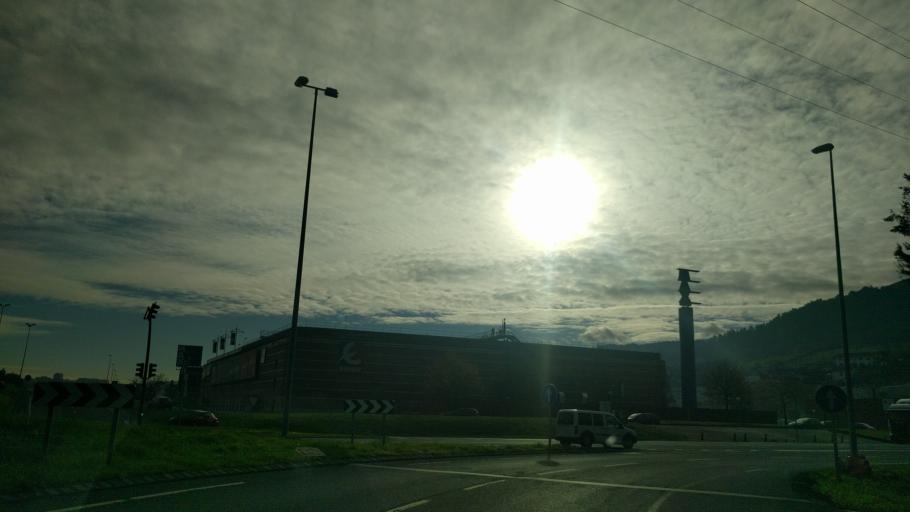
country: ES
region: Basque Country
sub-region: Bizkaia
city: Barakaldo
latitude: 43.2909
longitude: -3.0109
